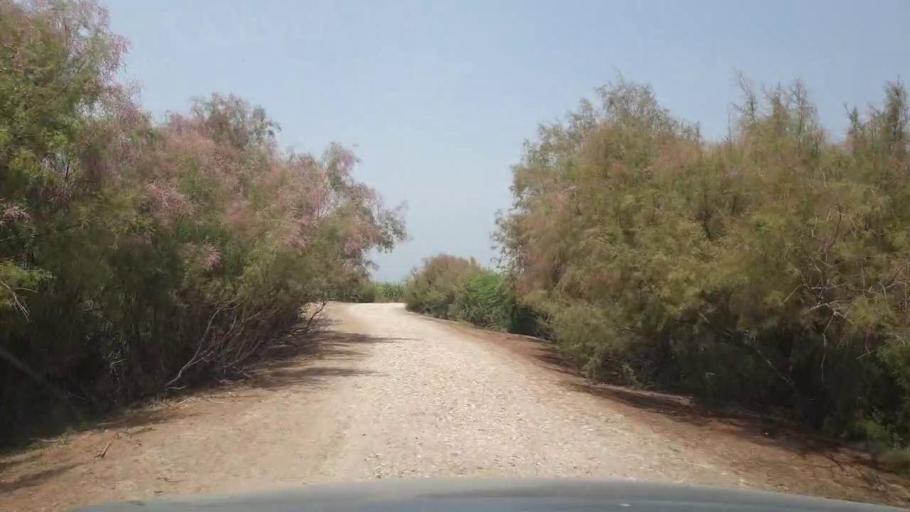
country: PK
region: Sindh
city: Garhi Yasin
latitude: 27.9520
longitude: 68.4359
